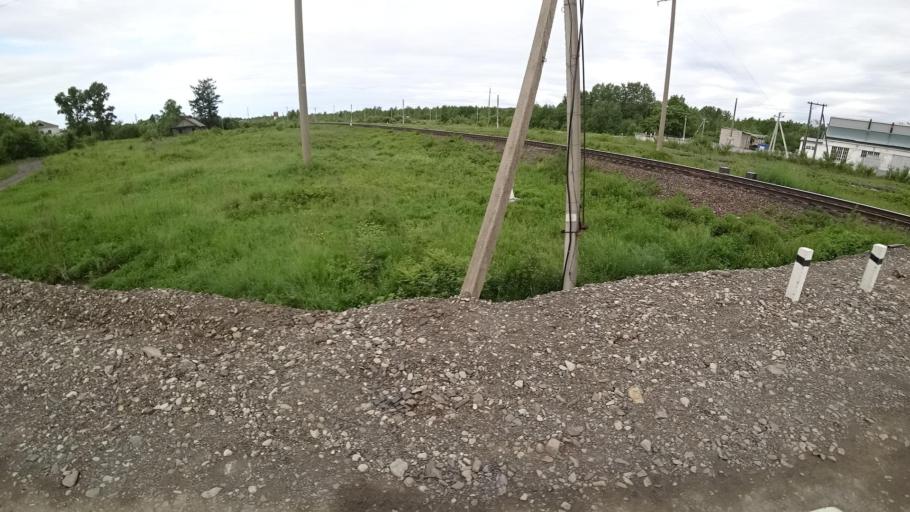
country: RU
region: Khabarovsk Krai
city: Amursk
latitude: 49.9039
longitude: 136.1437
